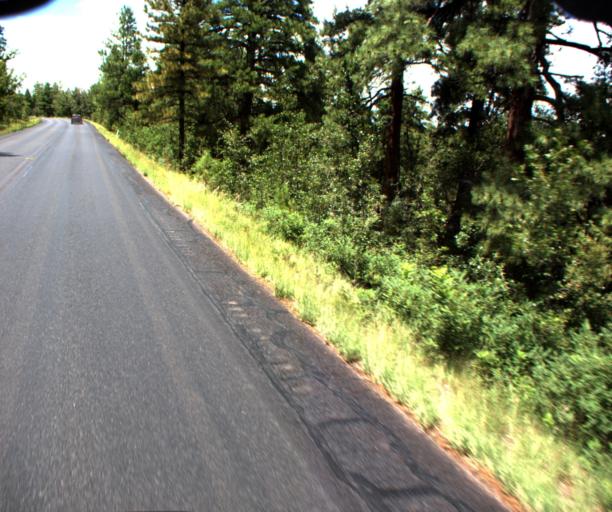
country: US
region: Arizona
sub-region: Gila County
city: Pine
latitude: 34.5109
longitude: -111.4807
